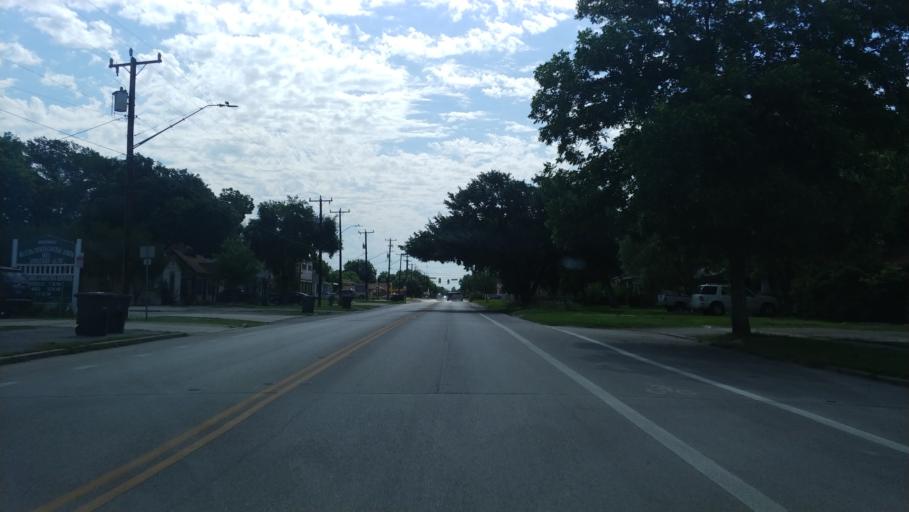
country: US
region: Texas
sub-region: Bexar County
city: San Antonio
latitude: 29.4498
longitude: -98.5266
